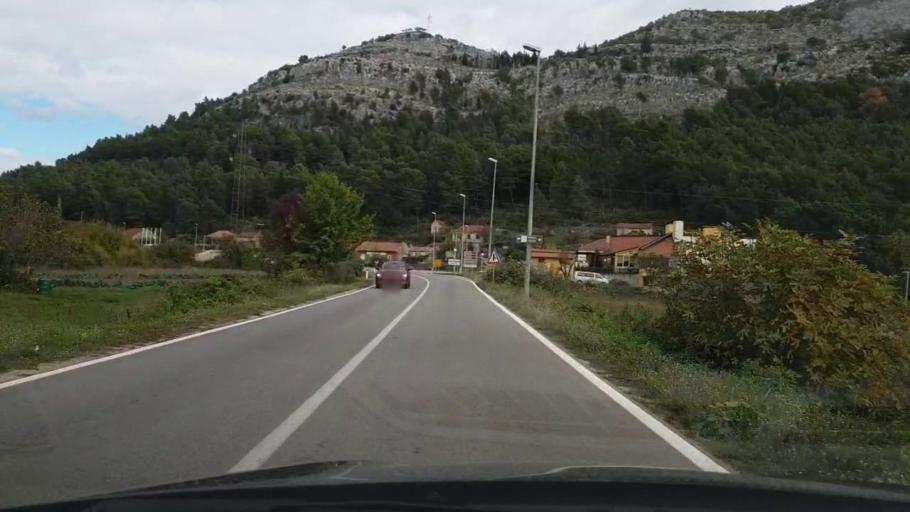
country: BA
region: Republika Srpska
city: Trebinje
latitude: 42.6884
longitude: 18.3343
